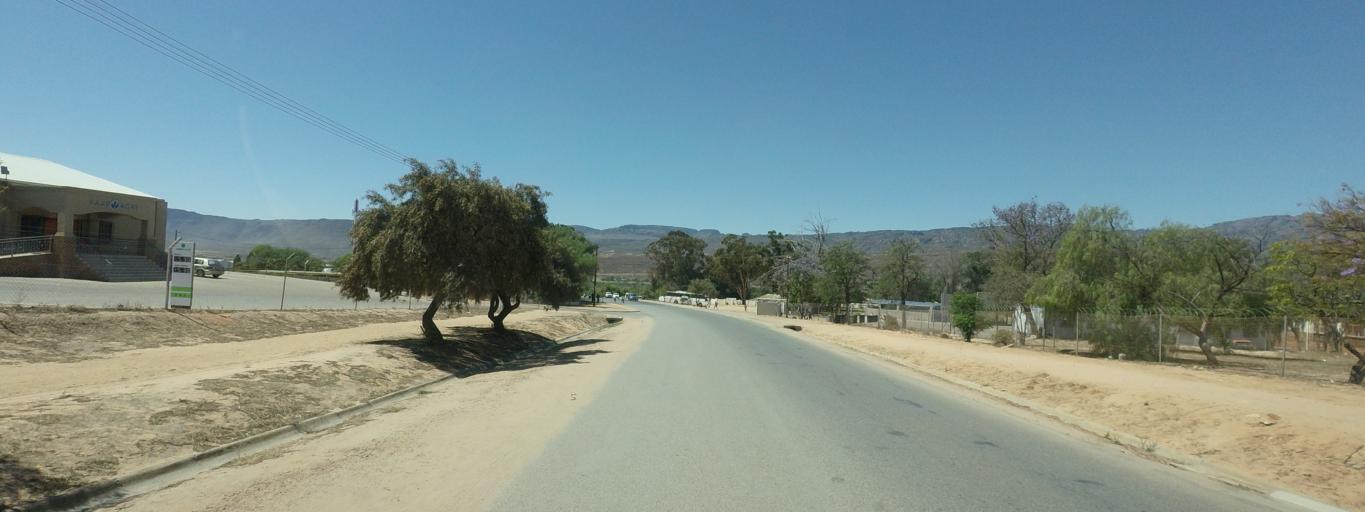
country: ZA
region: Western Cape
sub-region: West Coast District Municipality
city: Clanwilliam
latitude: -32.1885
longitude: 18.8893
